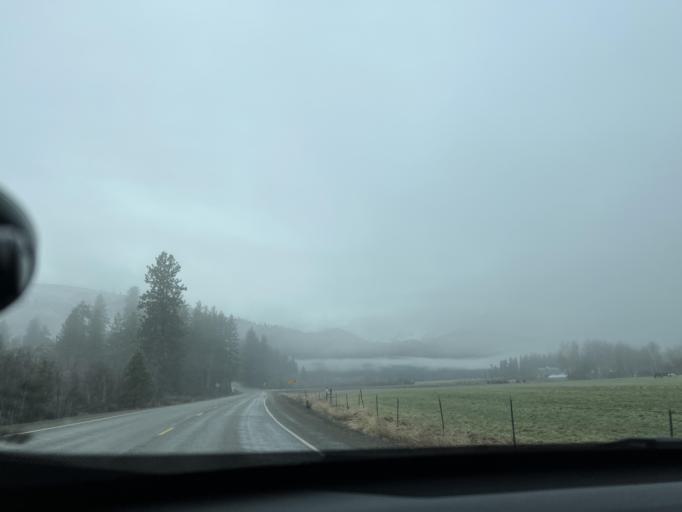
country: US
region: Washington
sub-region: Okanogan County
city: Brewster
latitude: 48.4697
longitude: -120.2002
